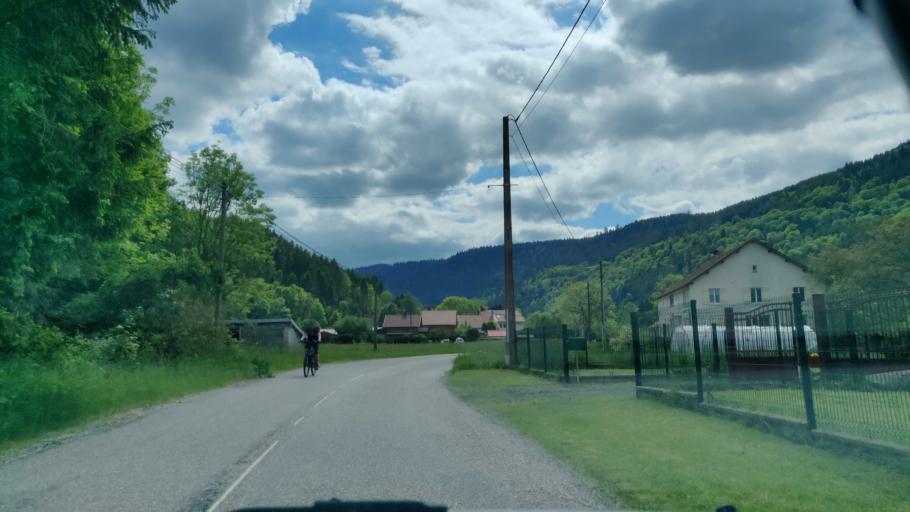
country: FR
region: Lorraine
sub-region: Departement des Vosges
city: Anould
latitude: 48.1392
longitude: 6.9675
